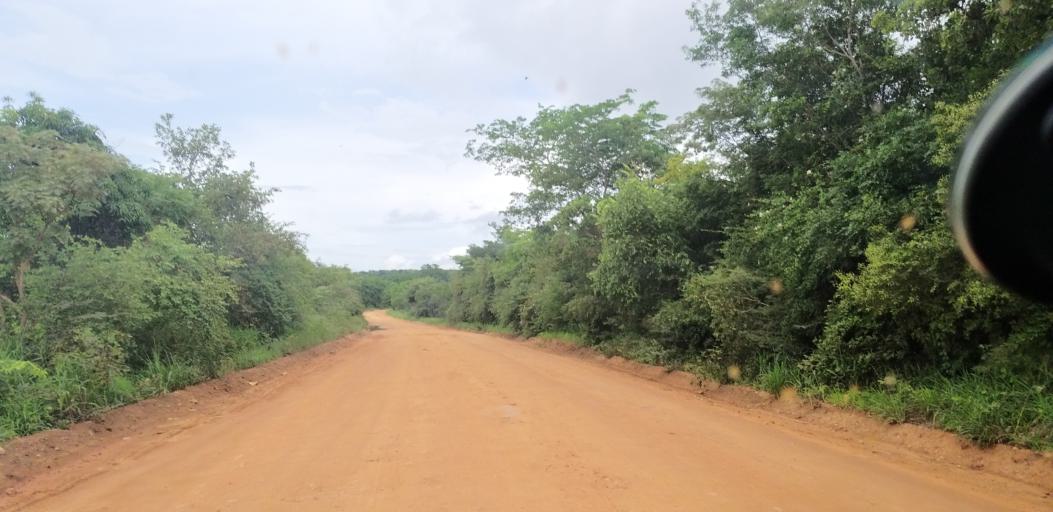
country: ZM
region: Lusaka
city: Lusaka
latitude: -15.1916
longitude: 28.4449
